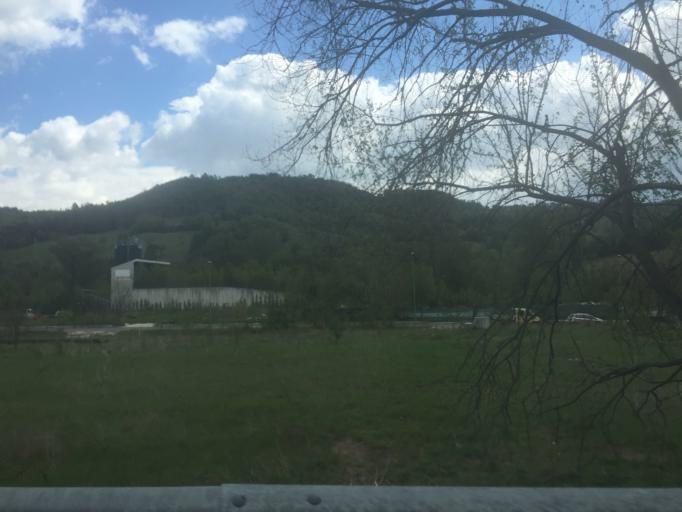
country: IT
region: The Marches
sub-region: Provincia di Macerata
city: Pieve Torina
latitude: 43.0507
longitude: 13.0547
